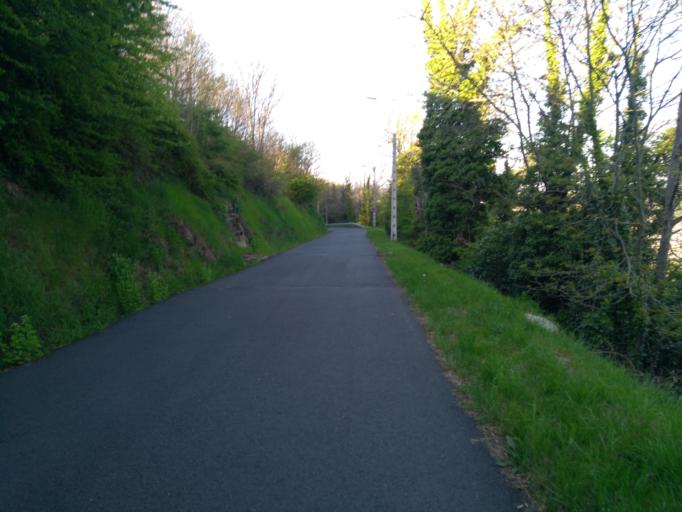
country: FR
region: Rhone-Alpes
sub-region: Departement de la Loire
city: Saint-Etienne
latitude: 45.4278
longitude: 4.4227
